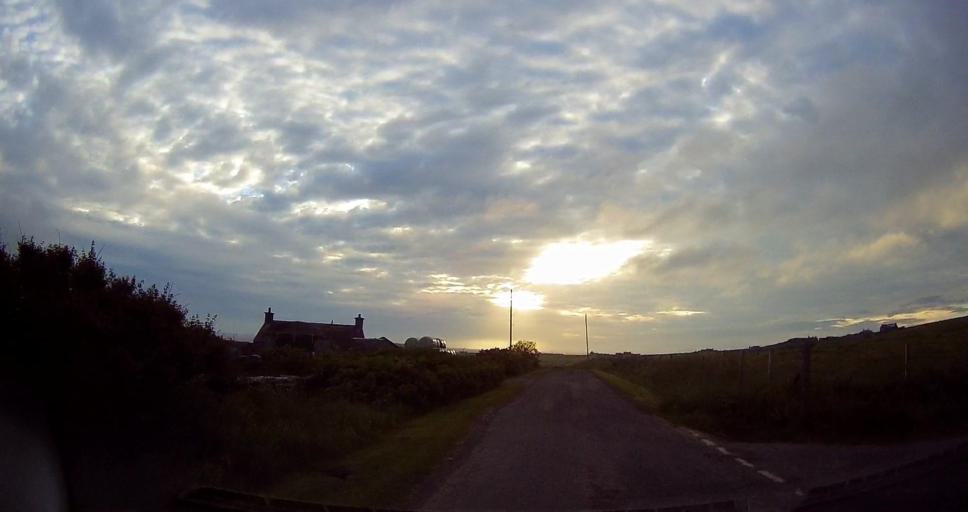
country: GB
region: Scotland
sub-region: Orkney Islands
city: Stromness
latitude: 59.1248
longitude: -3.2798
